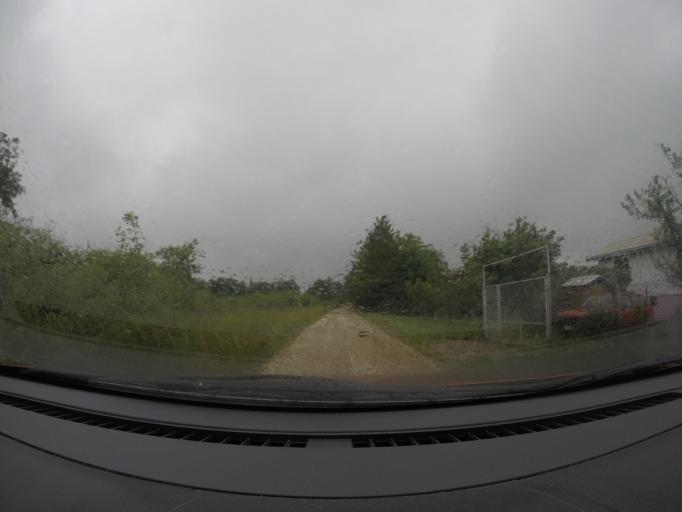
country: RS
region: Central Serbia
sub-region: Belgrade
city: Sopot
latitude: 44.5207
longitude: 20.5364
